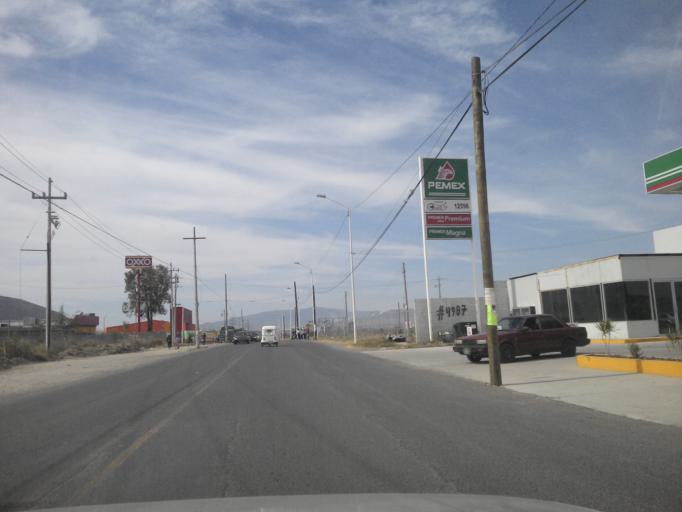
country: MX
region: Jalisco
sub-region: Tlajomulco de Zuniga
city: Colinas del Roble
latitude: 20.5092
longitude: -103.4005
